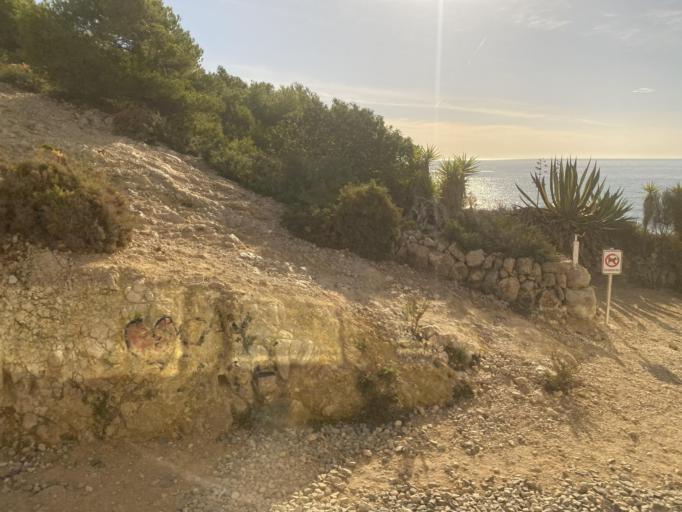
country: ES
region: Catalonia
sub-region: Provincia de Barcelona
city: Vilanova i la Geltru
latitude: 41.2204
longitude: 1.7642
